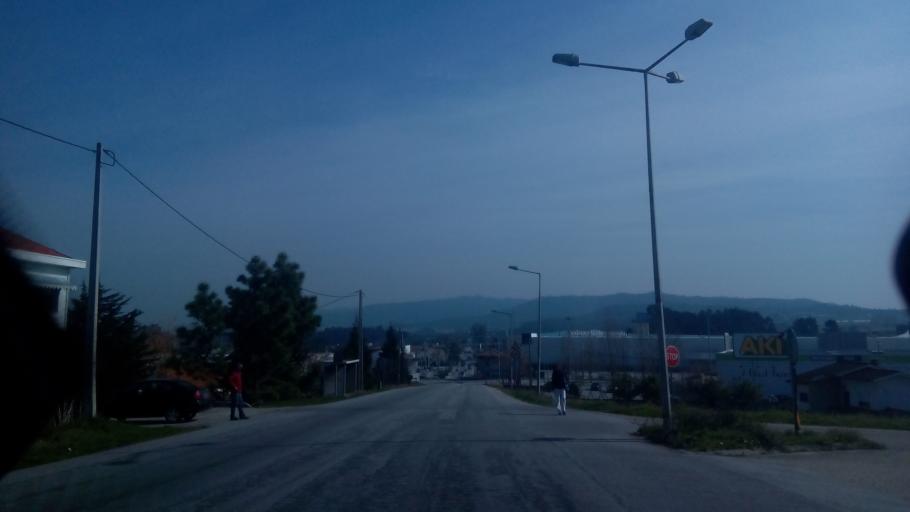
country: PT
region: Viana do Castelo
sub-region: Viana do Castelo
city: Darque
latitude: 41.6810
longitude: -8.7817
